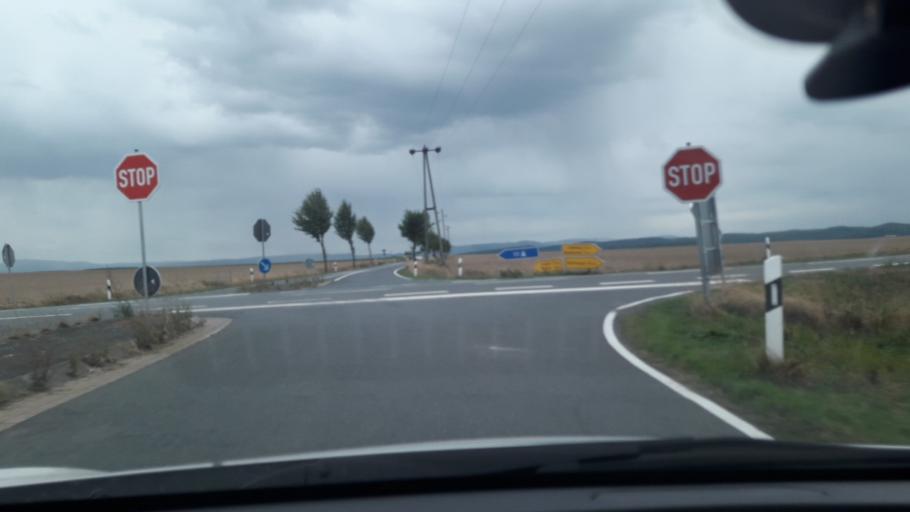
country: DE
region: Lower Saxony
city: Gielde
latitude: 52.0212
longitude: 10.5010
